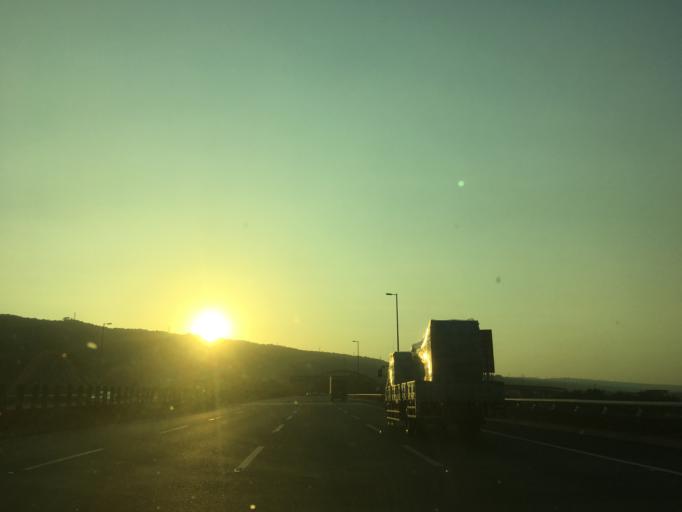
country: TW
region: Taiwan
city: Zhongxing New Village
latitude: 23.9562
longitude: 120.6600
